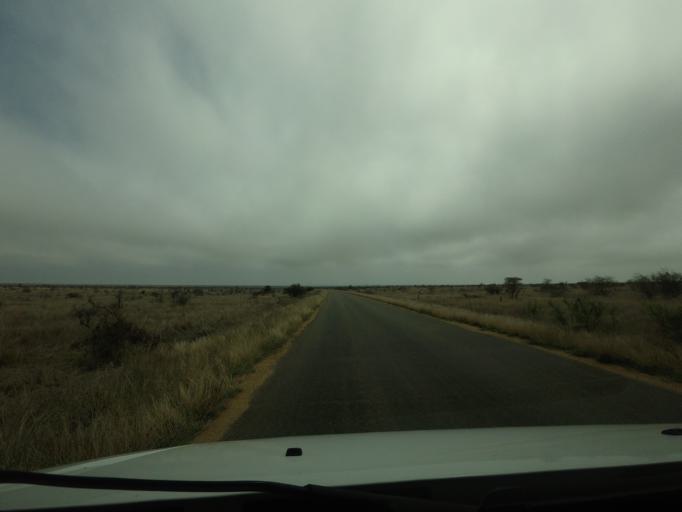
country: ZA
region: Limpopo
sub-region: Mopani District Municipality
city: Phalaborwa
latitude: -24.2142
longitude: 31.7199
